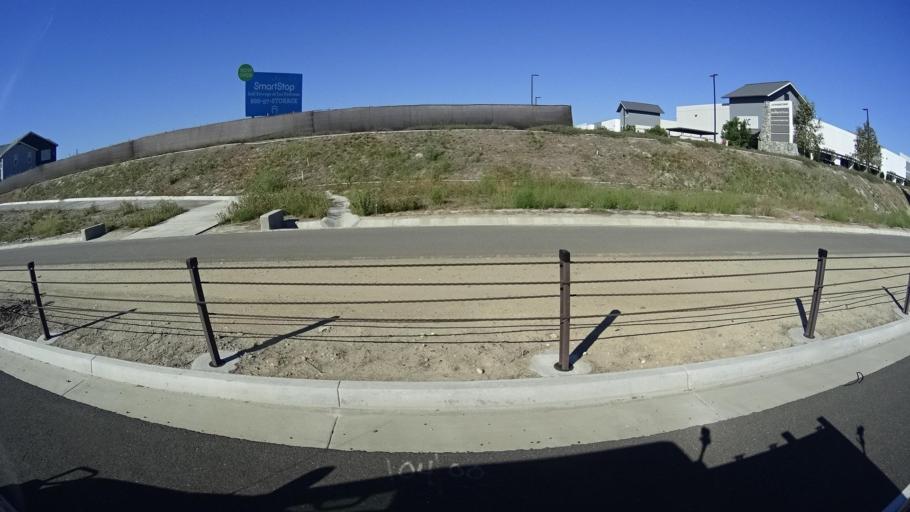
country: US
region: California
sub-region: Orange County
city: Ladera Ranch
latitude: 33.5521
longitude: -117.5948
